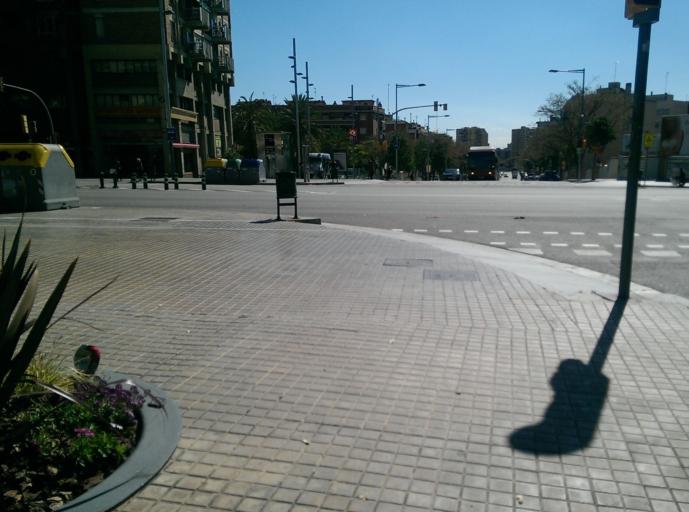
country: ES
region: Catalonia
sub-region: Provincia de Barcelona
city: Sant Andreu de Palomar
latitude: 41.4229
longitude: 2.1865
